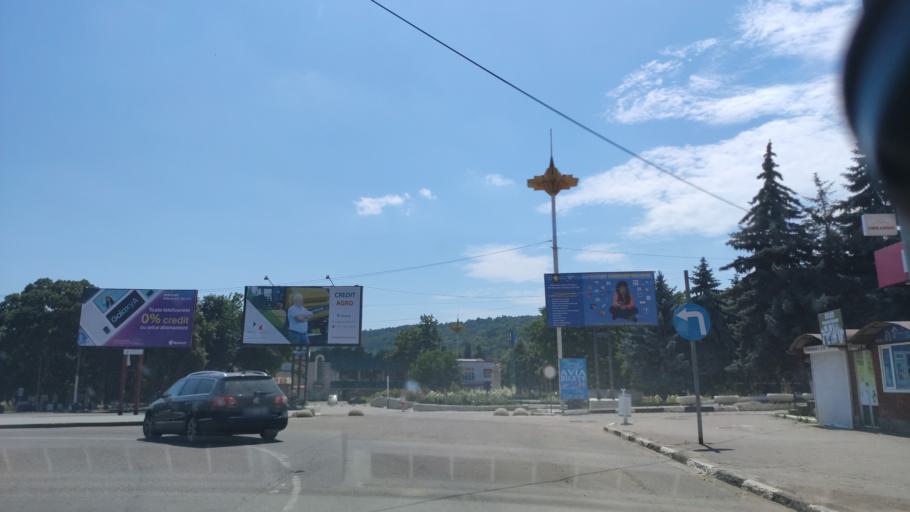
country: MD
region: Raionul Soroca
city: Soroca
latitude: 48.1577
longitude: 28.2995
